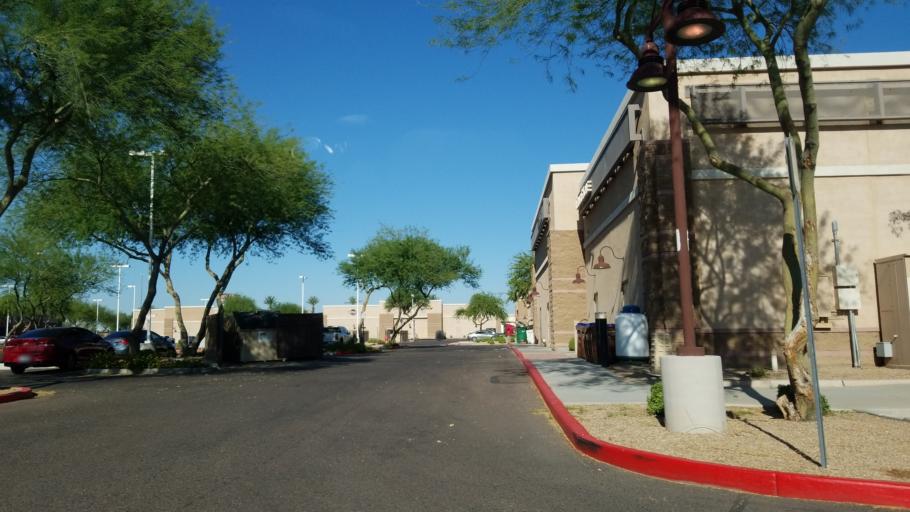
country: US
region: Arizona
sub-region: Maricopa County
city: Tolleson
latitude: 33.4641
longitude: -112.2701
